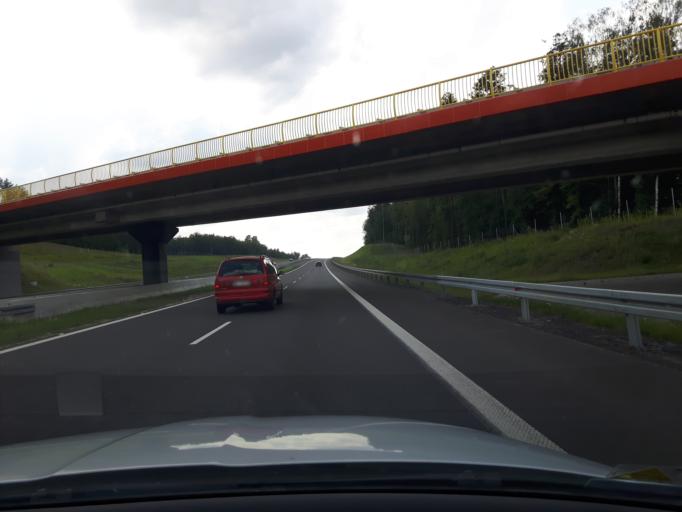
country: PL
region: Warmian-Masurian Voivodeship
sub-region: Powiat ostrodzki
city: Gierzwald
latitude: 53.5921
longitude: 20.1262
